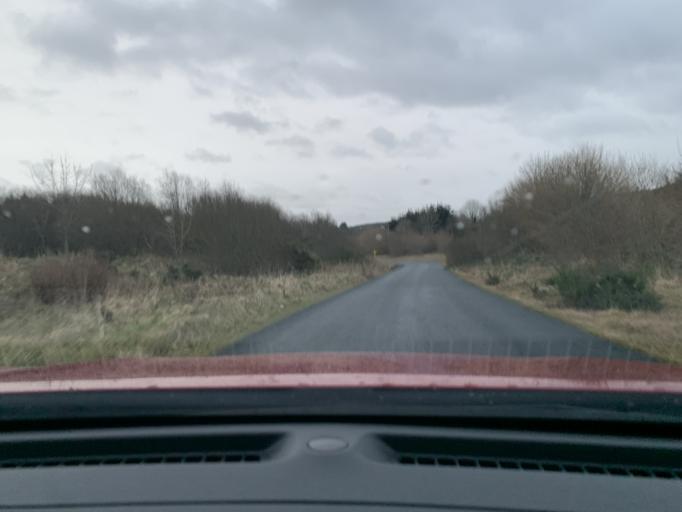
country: IE
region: Connaught
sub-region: Roscommon
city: Boyle
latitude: 54.0187
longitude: -8.3251
